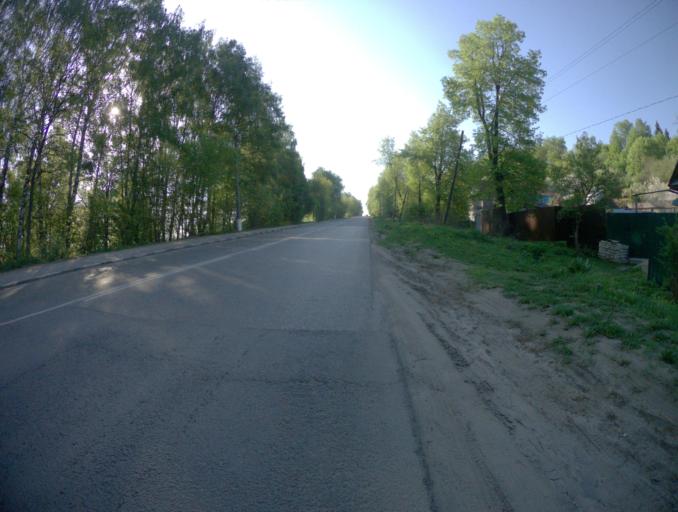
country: RU
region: Vladimir
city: Vyazniki
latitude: 56.2431
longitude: 42.1655
